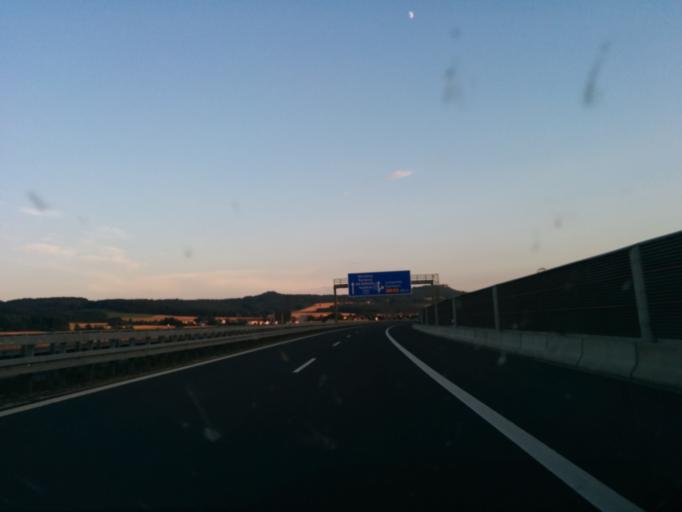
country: DE
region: Bavaria
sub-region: Upper Franconia
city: Lichtenfels
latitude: 50.1327
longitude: 11.0352
